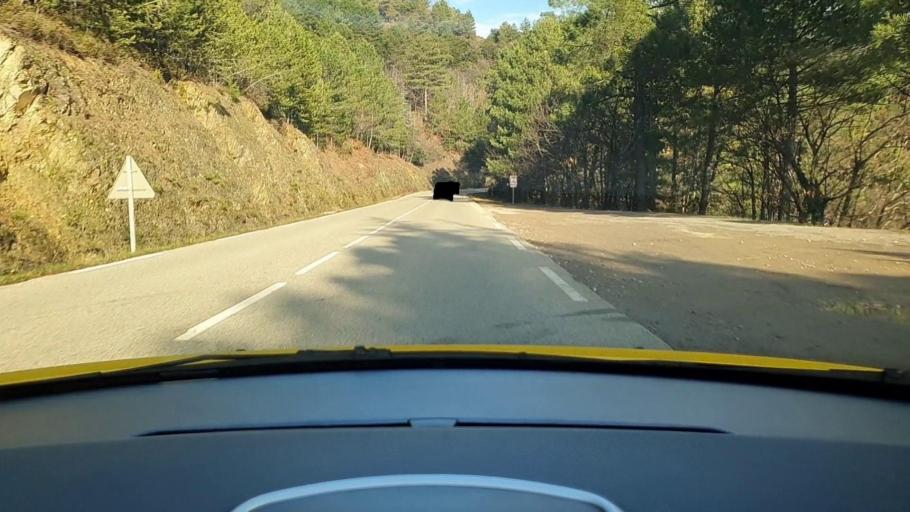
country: FR
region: Languedoc-Roussillon
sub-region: Departement du Gard
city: Branoux-les-Taillades
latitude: 44.3534
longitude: 3.9535
